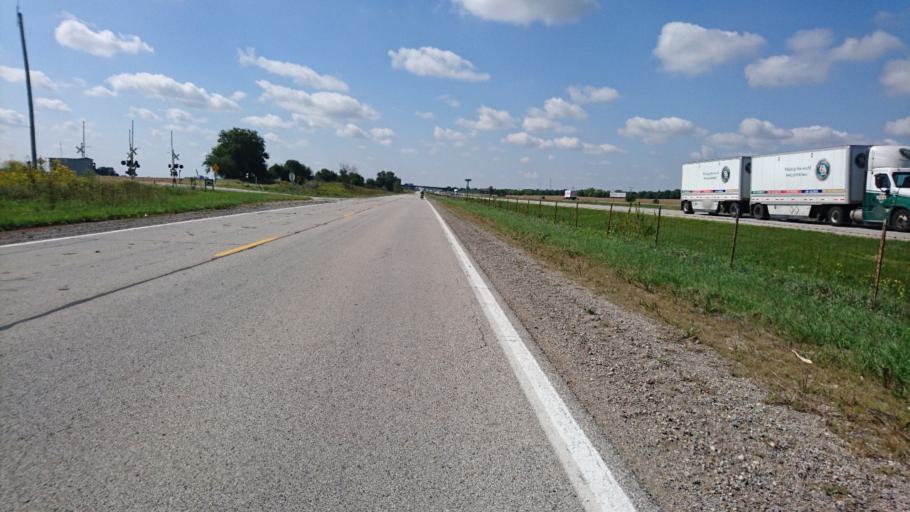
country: US
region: Illinois
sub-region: McLean County
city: Lexington
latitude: 40.6100
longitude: -88.8314
